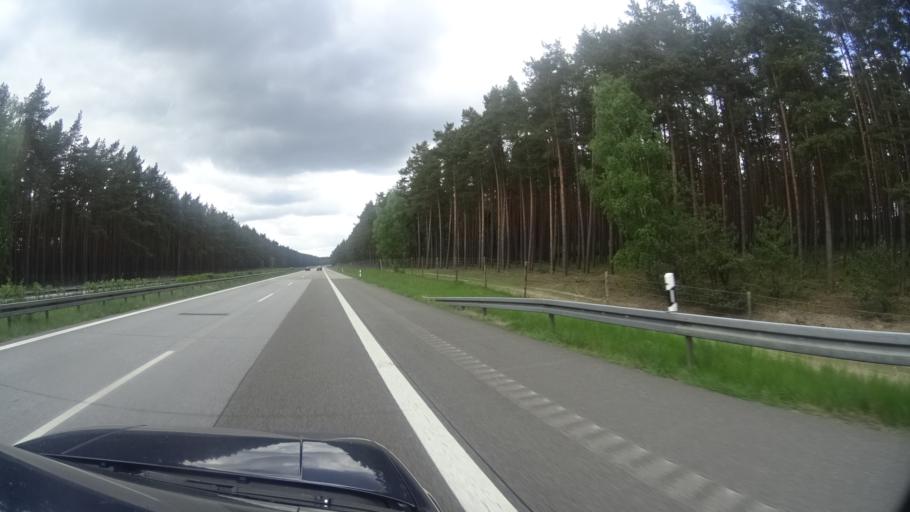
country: DE
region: Mecklenburg-Vorpommern
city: Plau am See
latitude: 53.5457
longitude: 12.3330
